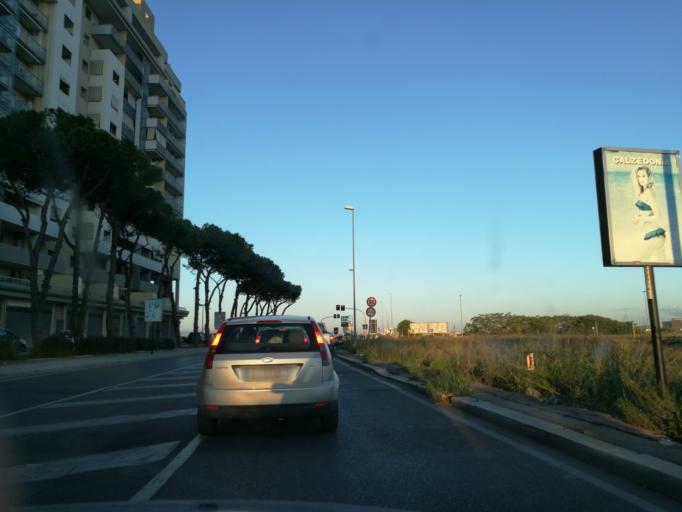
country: IT
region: Apulia
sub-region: Provincia di Bari
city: San Paolo
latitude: 41.1232
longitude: 16.8043
